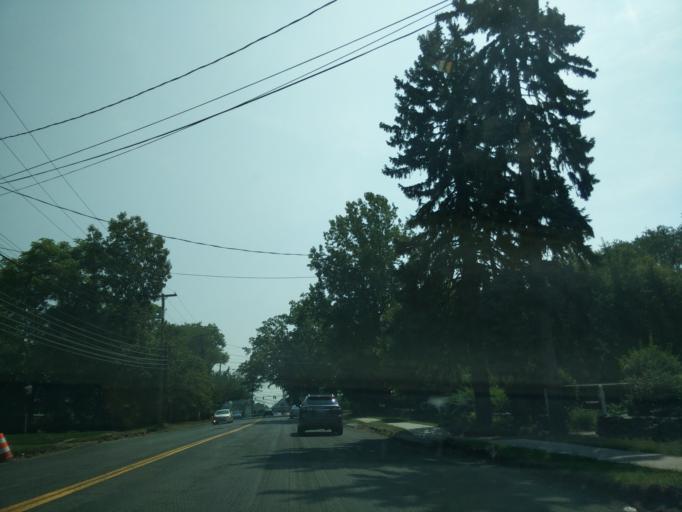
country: US
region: Connecticut
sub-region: Fairfield County
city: Bridgeport
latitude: 41.1792
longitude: -73.2449
